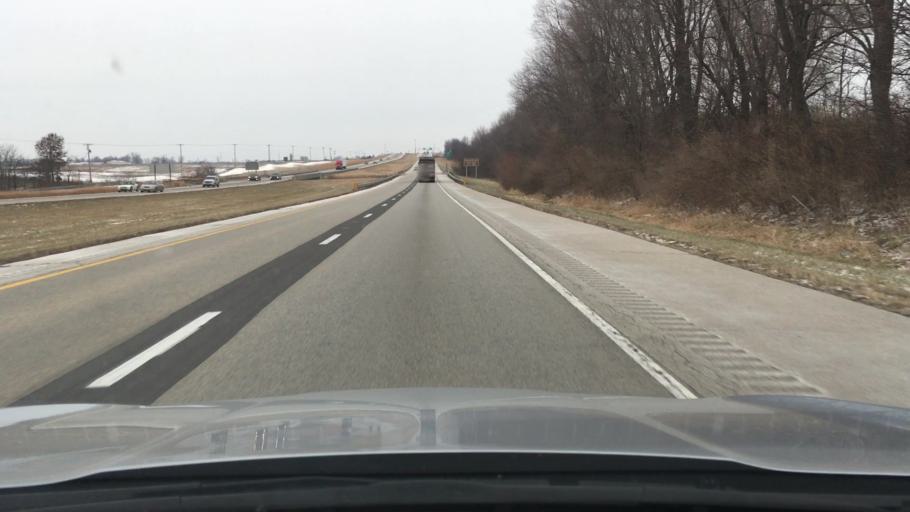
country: US
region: Illinois
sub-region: Sangamon County
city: Divernon
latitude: 39.5781
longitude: -89.6462
